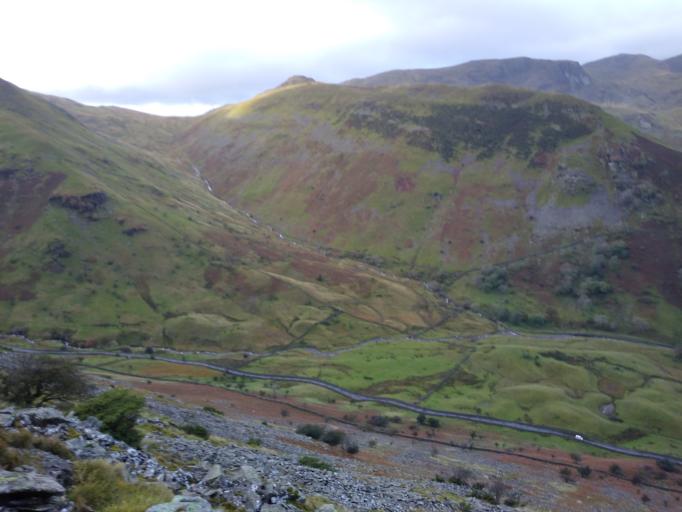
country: GB
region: England
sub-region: Cumbria
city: Ambleside
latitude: 54.4900
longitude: -2.9190
